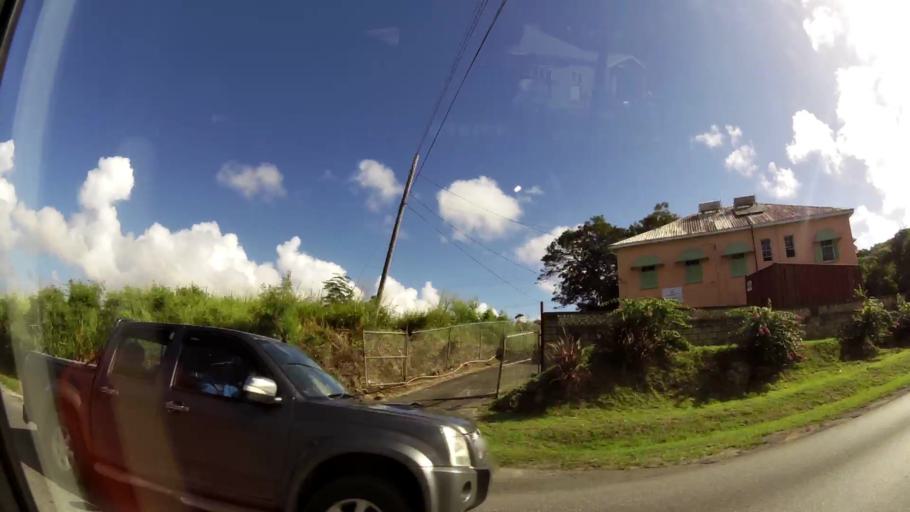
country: BB
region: Saint James
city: Holetown
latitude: 13.1997
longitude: -59.6150
